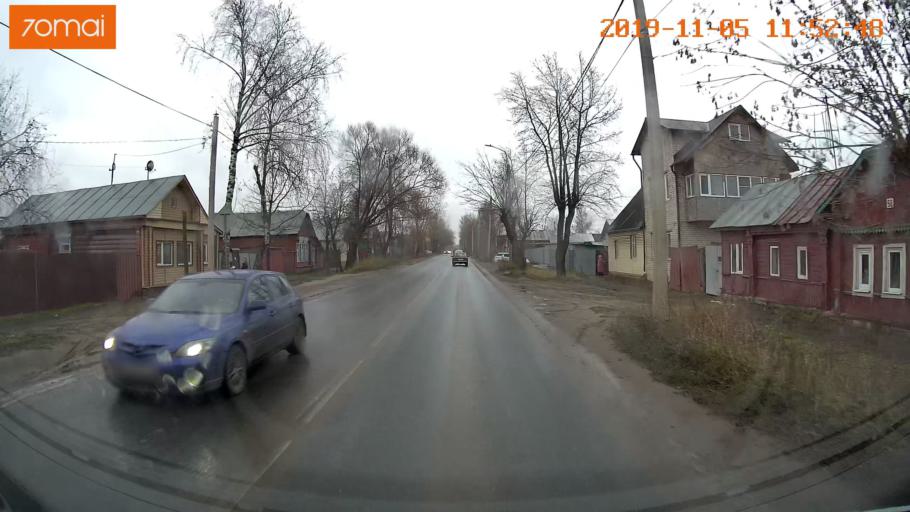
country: RU
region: Ivanovo
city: Bogorodskoye
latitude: 56.9983
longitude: 41.0298
